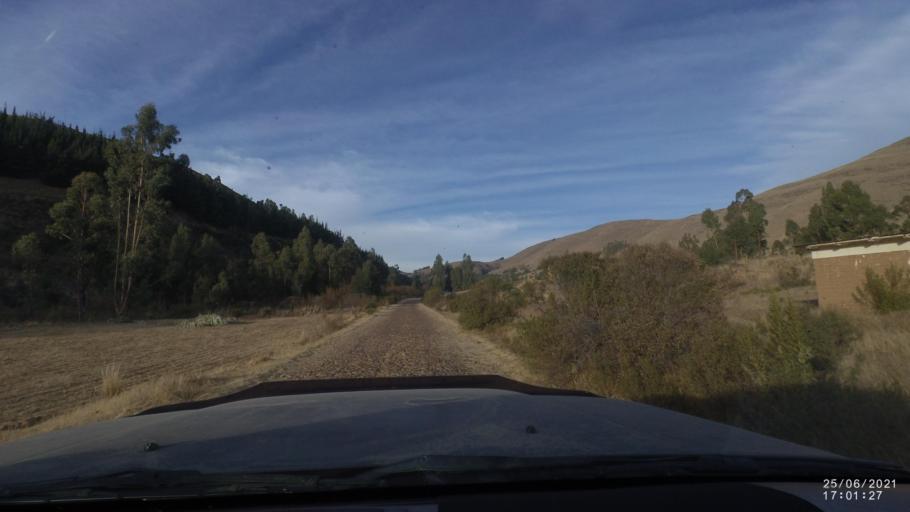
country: BO
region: Cochabamba
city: Arani
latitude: -17.8374
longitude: -65.7410
